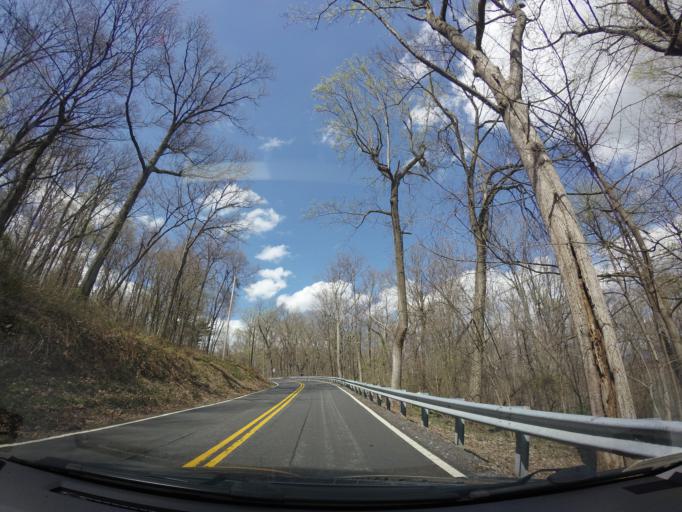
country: US
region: Maryland
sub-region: Frederick County
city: Brunswick
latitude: 39.4042
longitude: -77.6379
